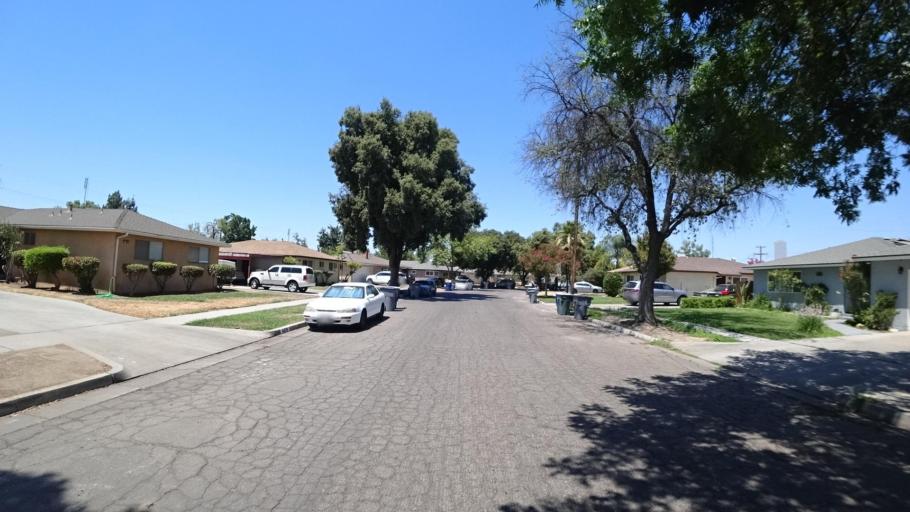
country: US
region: California
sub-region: Fresno County
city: Sunnyside
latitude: 36.7604
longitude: -119.7328
